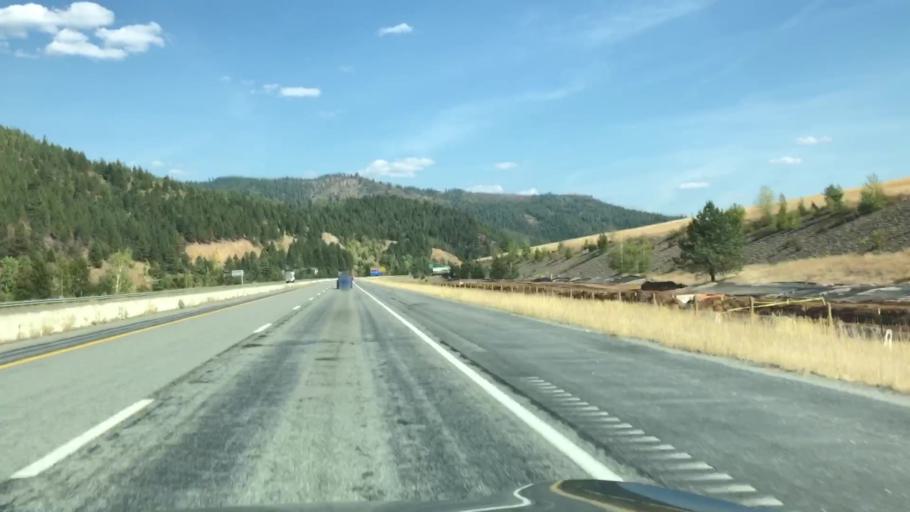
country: US
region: Idaho
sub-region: Shoshone County
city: Kellogg
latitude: 47.5482
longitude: -116.1461
